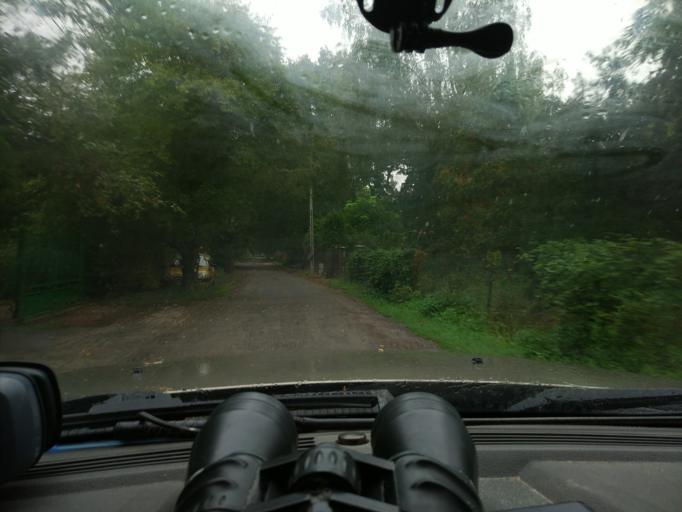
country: PL
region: Masovian Voivodeship
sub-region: Powiat grodziski
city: Podkowa Lesna
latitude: 52.1284
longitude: 20.7347
